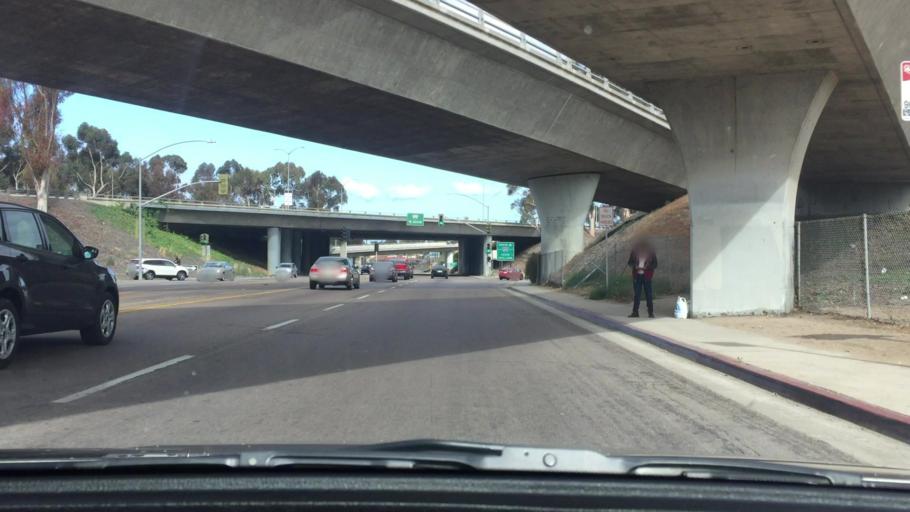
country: US
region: California
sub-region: San Diego County
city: Chula Vista
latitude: 32.6606
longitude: -117.0751
